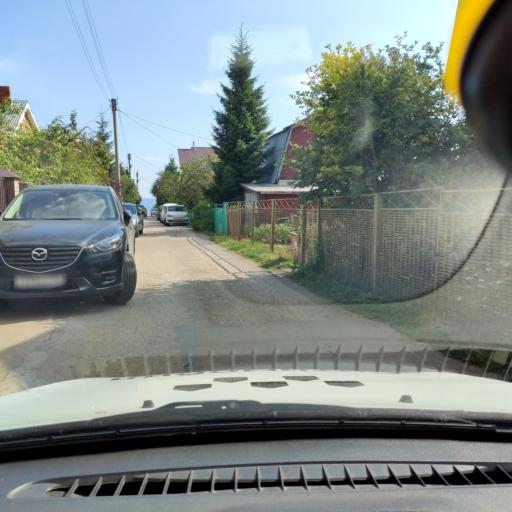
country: RU
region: Samara
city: Podstepki
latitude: 53.5042
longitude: 49.1440
